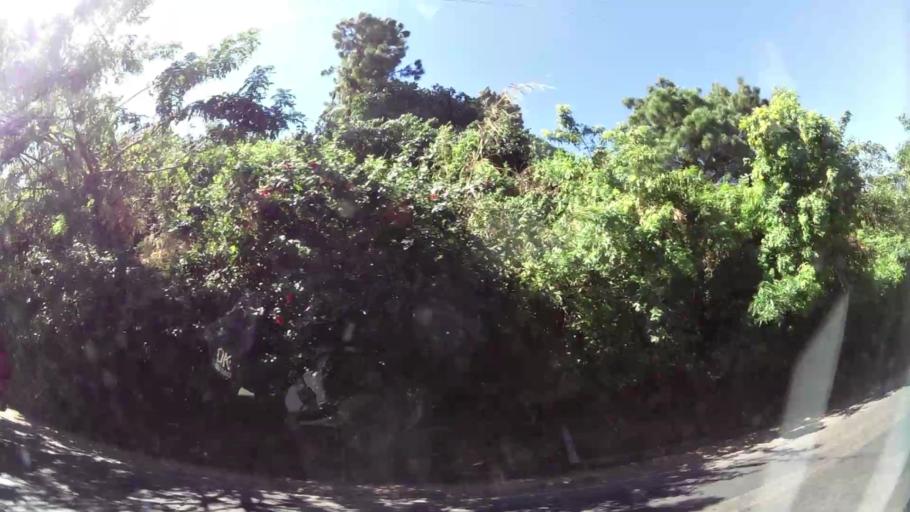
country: SV
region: Ahuachapan
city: Ahuachapan
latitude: 13.9147
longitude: -89.8379
